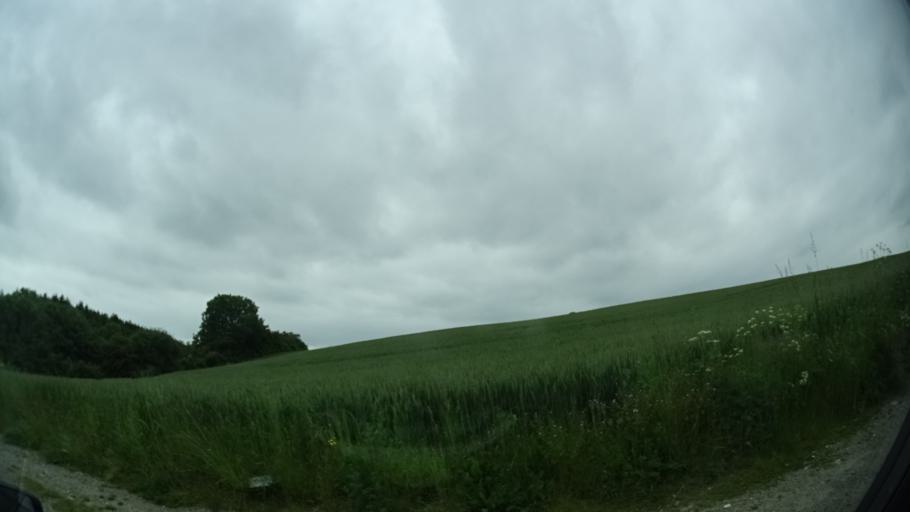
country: DK
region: Central Jutland
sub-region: Arhus Kommune
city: Kolt
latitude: 56.0955
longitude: 10.0718
